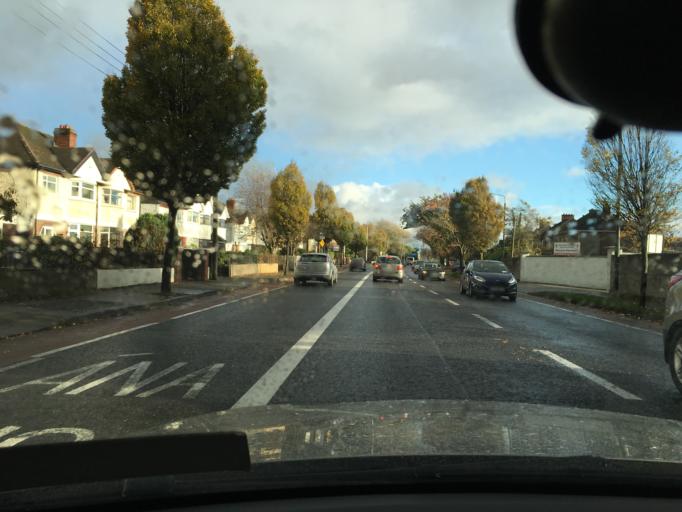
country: IE
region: Leinster
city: Cabra
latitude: 53.3674
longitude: -6.3160
